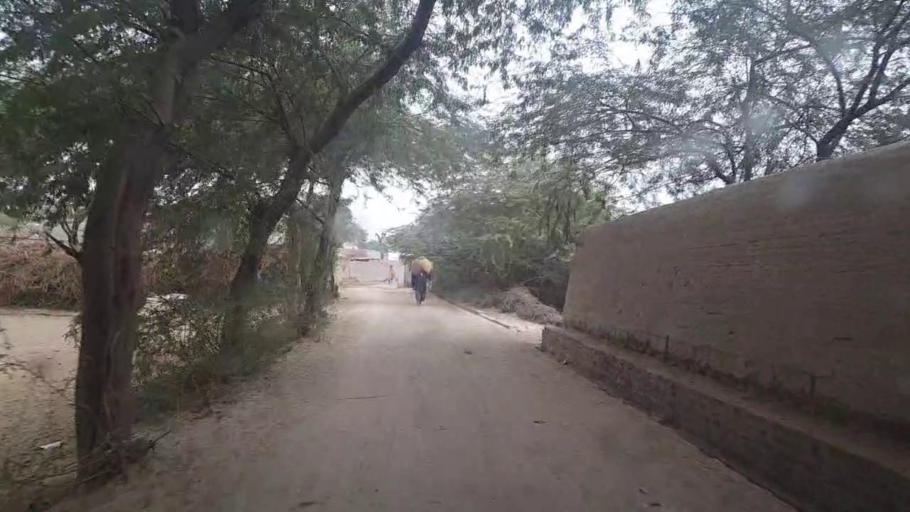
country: PK
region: Sindh
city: Gambat
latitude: 27.3581
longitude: 68.5977
